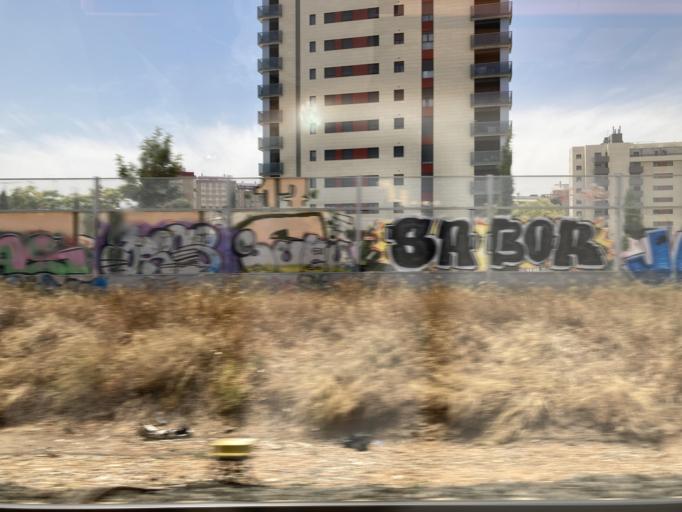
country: ES
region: Andalusia
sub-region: Provincia de Sevilla
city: Sevilla
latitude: 37.3550
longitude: -5.9727
